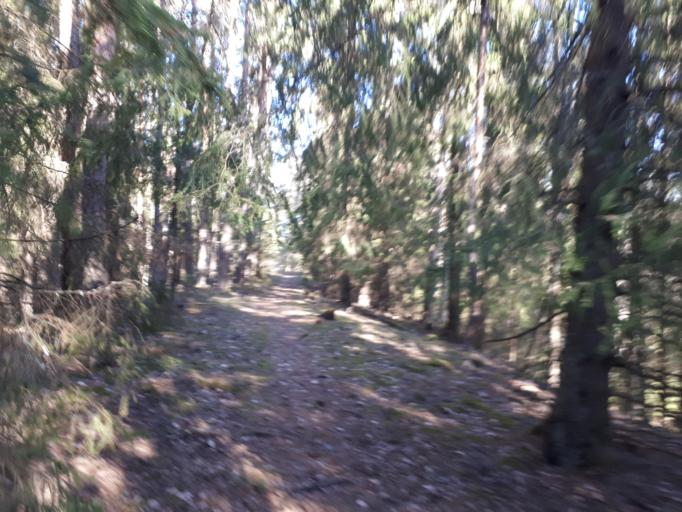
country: SE
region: Soedermanland
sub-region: Flens Kommun
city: Halleforsnas
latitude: 59.0828
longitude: 16.3662
